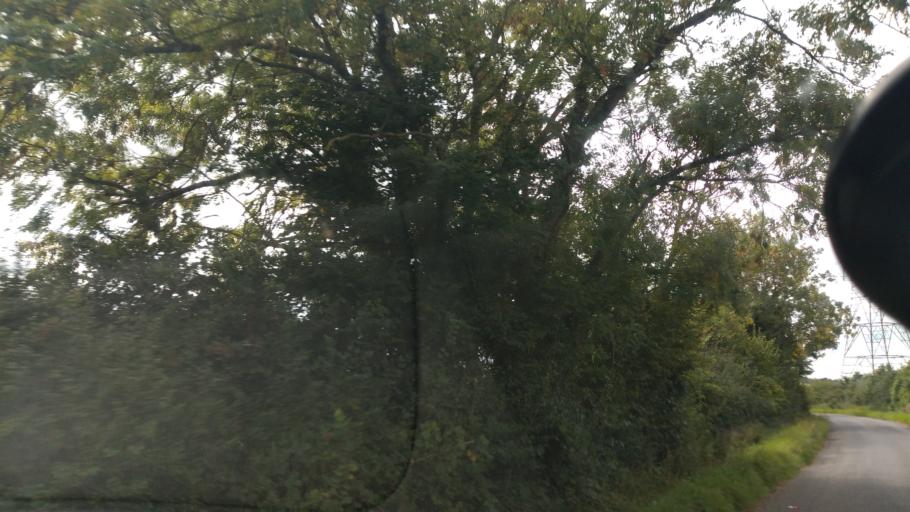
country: GB
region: England
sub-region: Wiltshire
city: Chippenham
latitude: 51.4416
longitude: -2.1497
